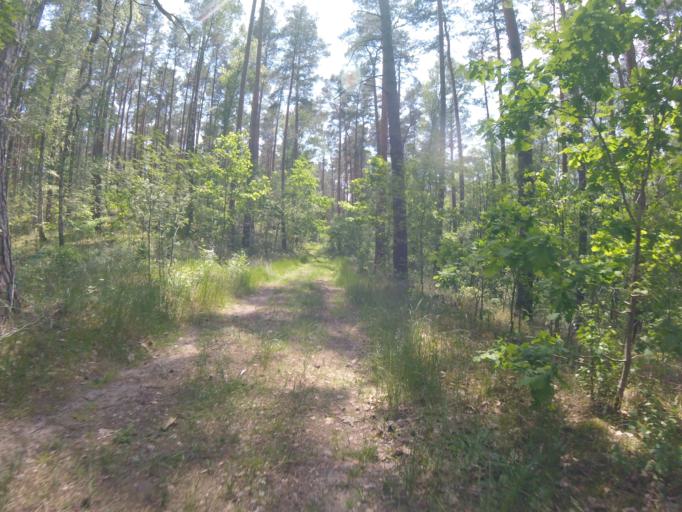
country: DE
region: Brandenburg
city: Teupitz
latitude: 52.1071
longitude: 13.5969
